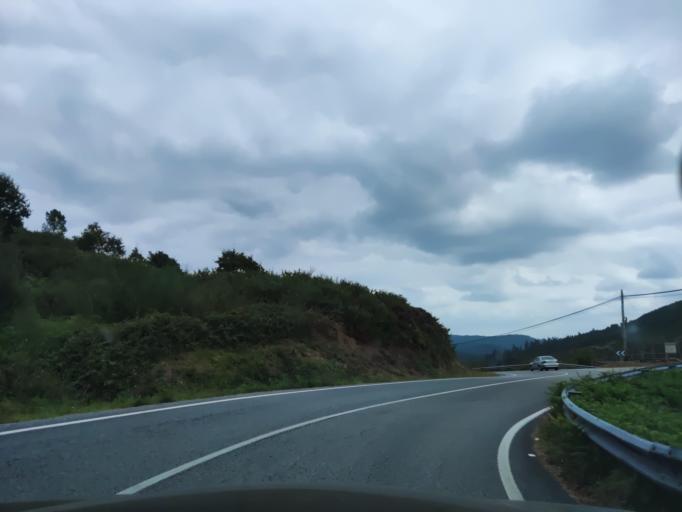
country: ES
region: Galicia
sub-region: Provincia da Coruna
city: Padron
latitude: 42.7420
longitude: -8.6257
